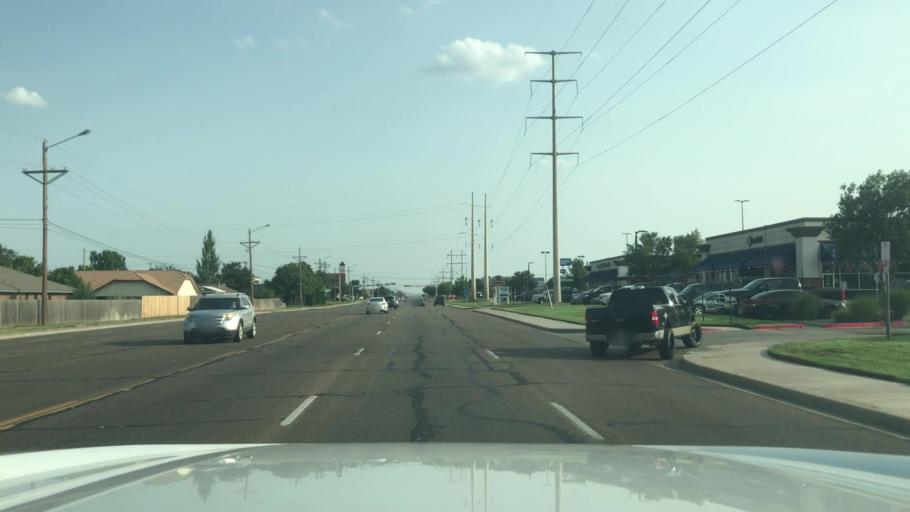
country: US
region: Texas
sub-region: Potter County
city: Amarillo
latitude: 35.1797
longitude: -101.9383
